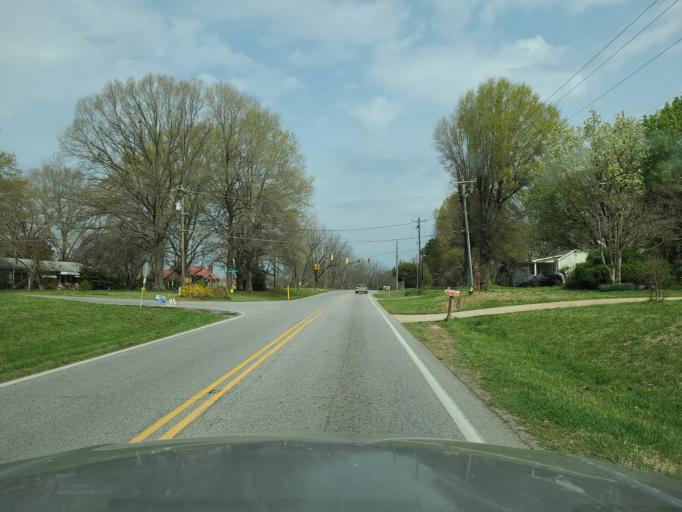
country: US
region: North Carolina
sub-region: Gaston County
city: Stanley
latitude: 35.3360
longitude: -81.0914
